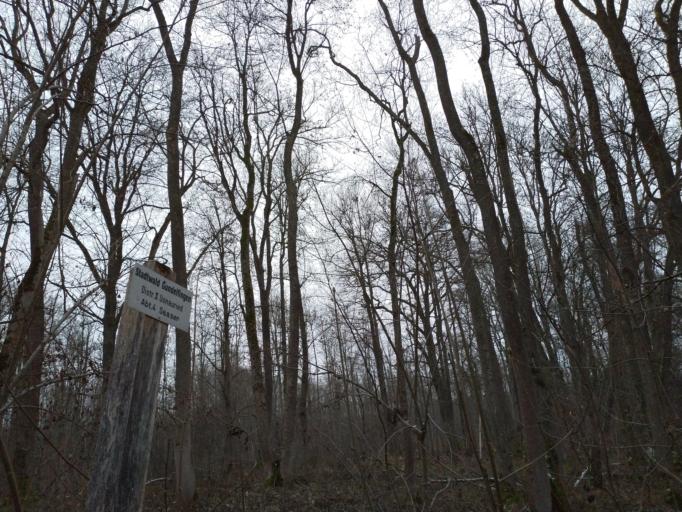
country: DE
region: Bavaria
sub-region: Swabia
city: Offingen
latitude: 48.4867
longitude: 10.3363
